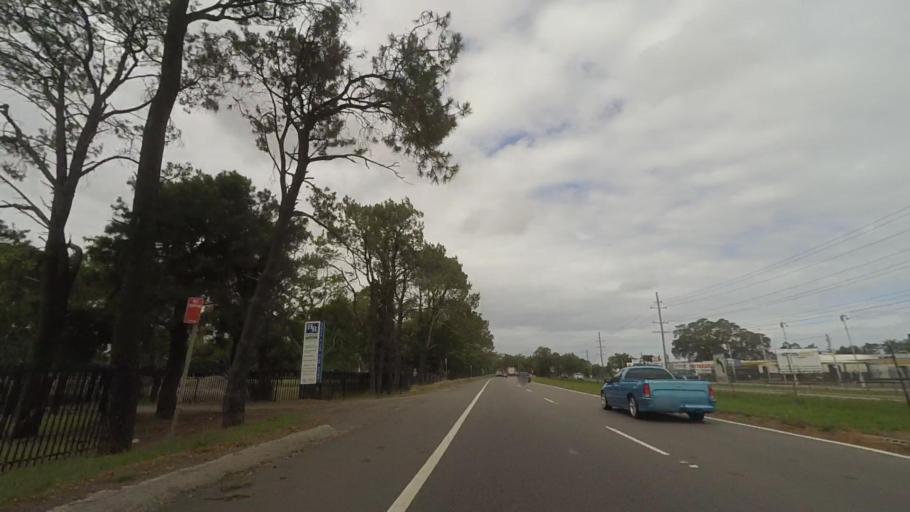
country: AU
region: New South Wales
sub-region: Port Stephens Shire
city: Raymond Terrace
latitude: -32.7838
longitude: 151.7343
